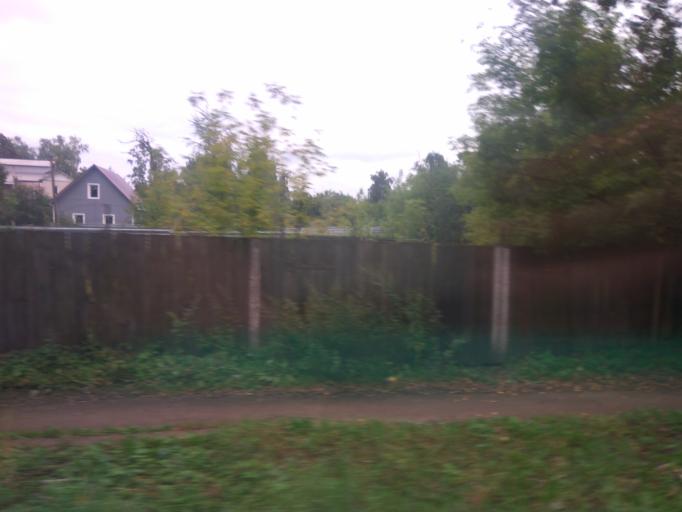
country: RU
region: Moscow
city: Zhulebino
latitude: 55.6957
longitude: 37.8721
